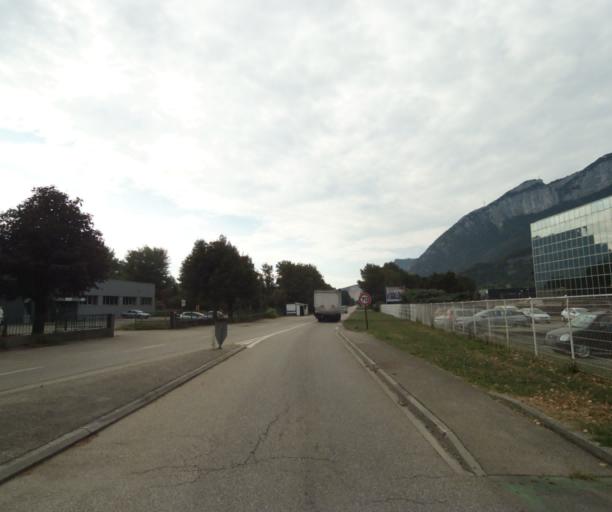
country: FR
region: Rhone-Alpes
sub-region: Departement de l'Isere
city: Noyarey
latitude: 45.2592
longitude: 5.6262
